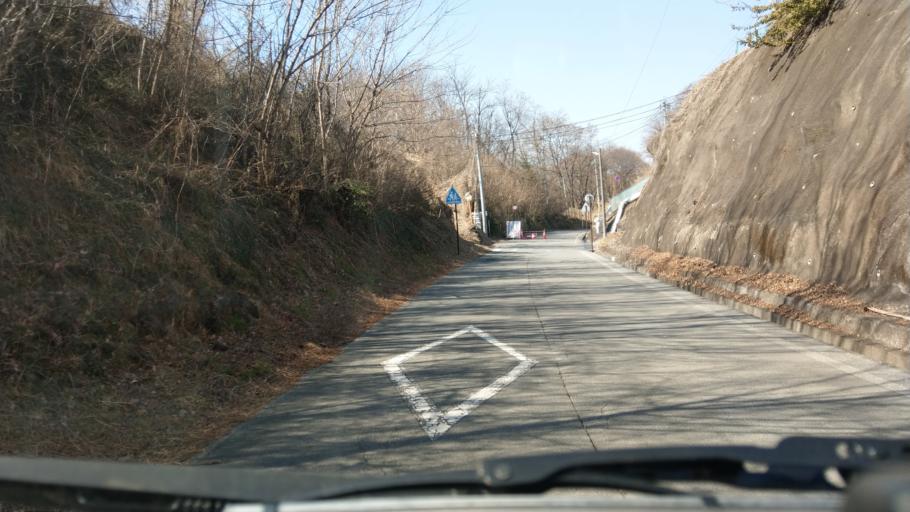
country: JP
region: Nagano
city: Komoro
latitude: 36.3336
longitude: 138.4059
